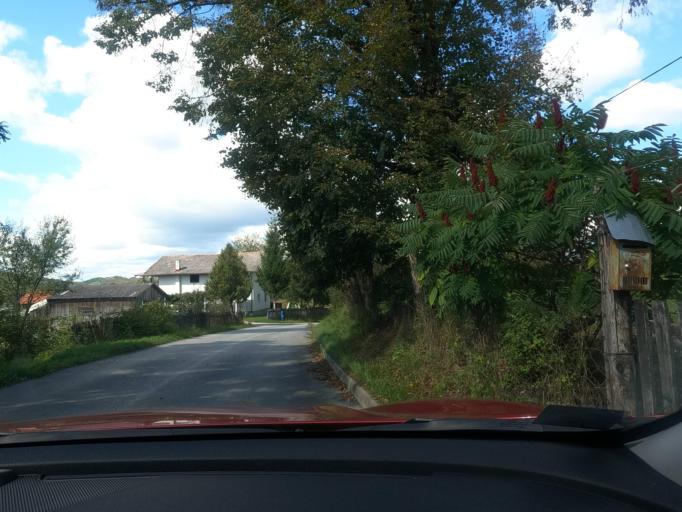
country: BA
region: Federation of Bosnia and Herzegovina
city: Velika Kladusa
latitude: 45.2112
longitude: 15.8184
